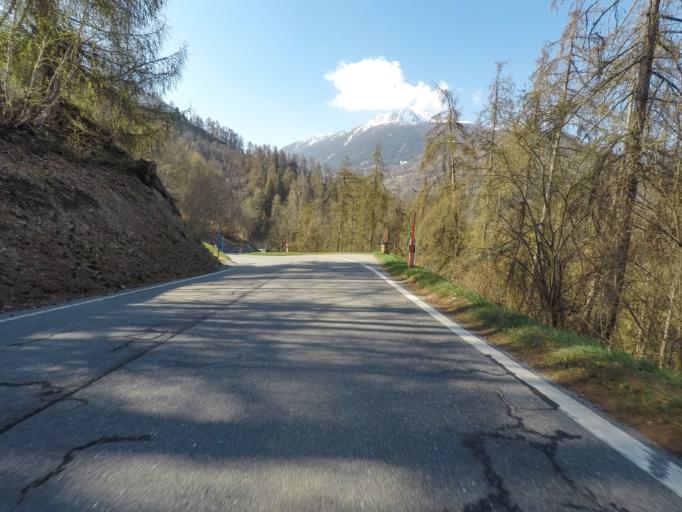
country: CH
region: Valais
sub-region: Conthey District
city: Basse-Nendaz
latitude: 46.1878
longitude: 7.3304
